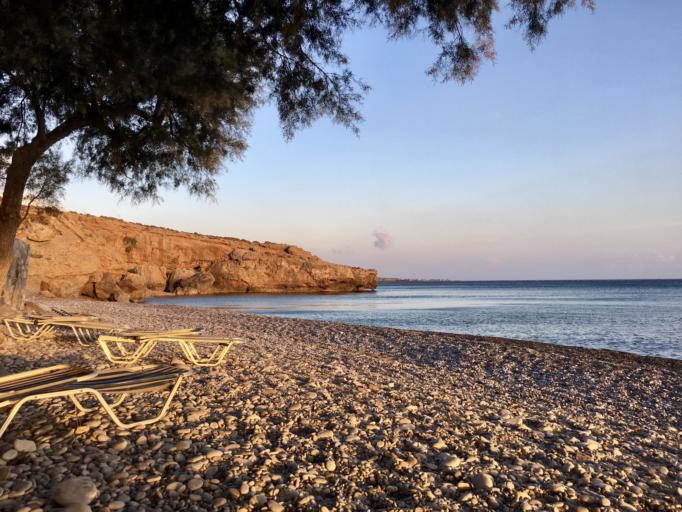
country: GR
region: Crete
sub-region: Nomos Chanias
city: Chora Sfakion
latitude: 35.2000
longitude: 24.1908
